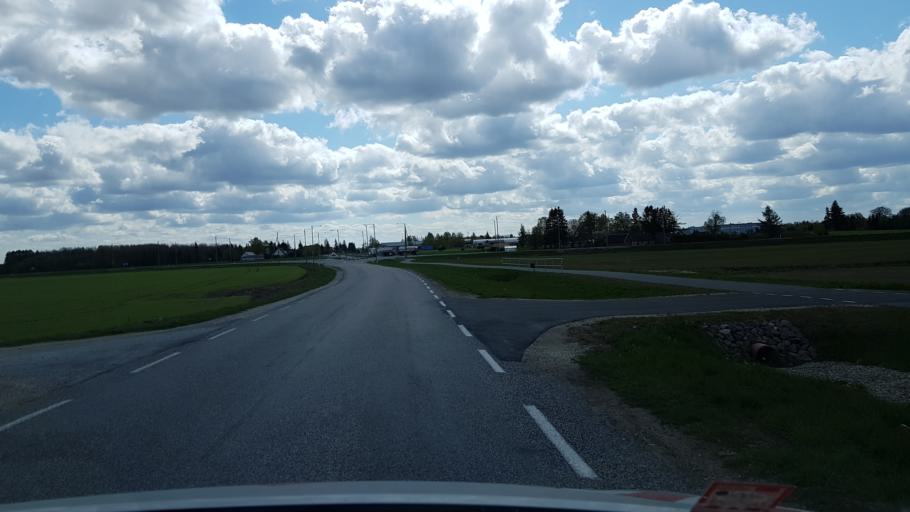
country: EE
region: Jogevamaa
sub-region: Poltsamaa linn
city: Poltsamaa
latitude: 58.6729
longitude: 25.9617
